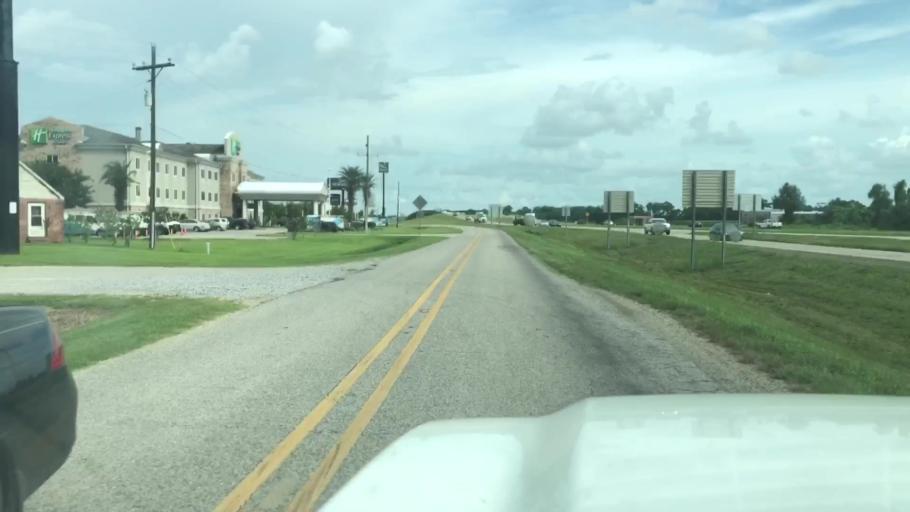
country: US
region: Louisiana
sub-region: Iberia Parish
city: New Iberia
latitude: 29.9839
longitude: -91.8568
